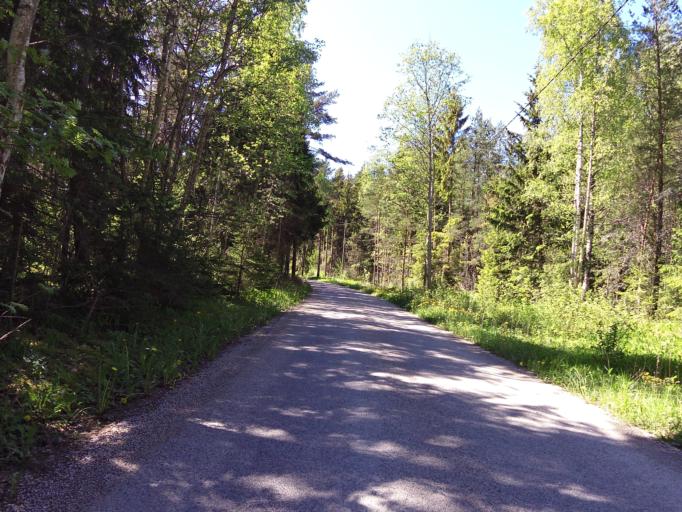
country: EE
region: Harju
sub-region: Paldiski linn
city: Paldiski
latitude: 59.2687
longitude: 23.7661
